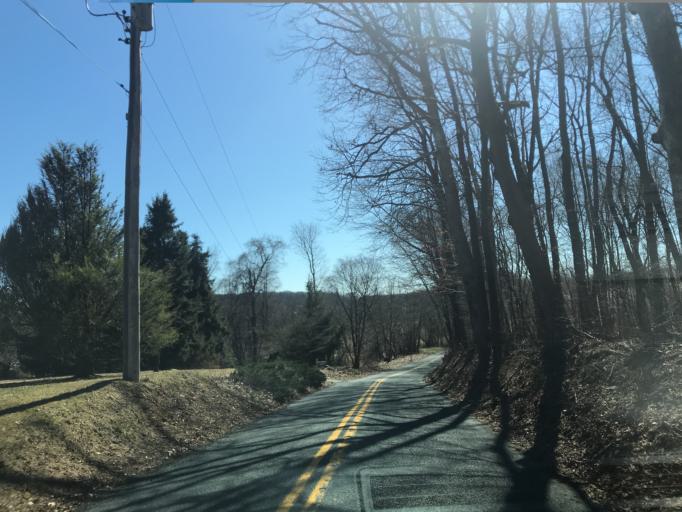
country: US
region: Pennsylvania
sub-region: York County
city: Stewartstown
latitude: 39.7110
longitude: -76.5240
